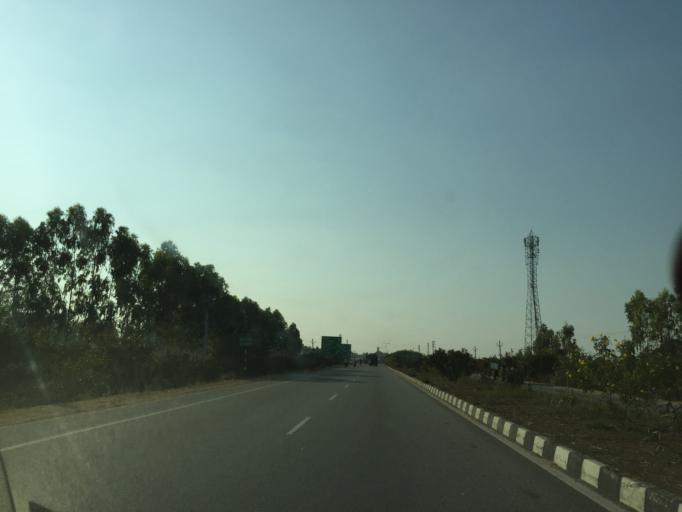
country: IN
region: Telangana
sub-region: Nalgonda
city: Bhongir
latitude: 17.5024
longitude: 78.8771
